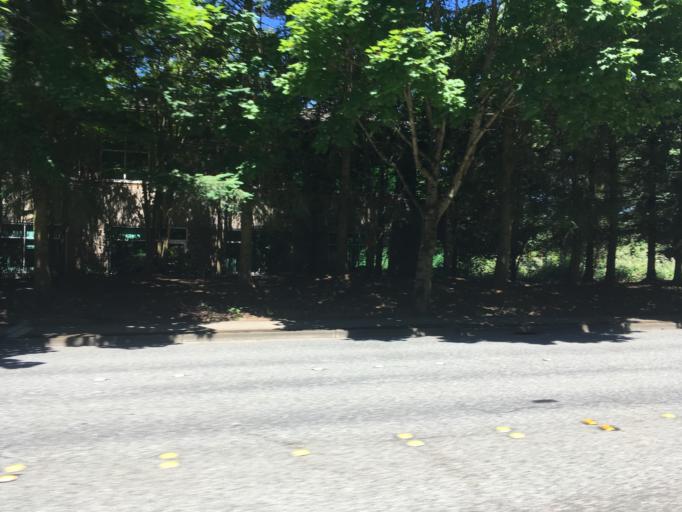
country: US
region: Washington
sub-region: King County
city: Redmond
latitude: 47.6346
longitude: -122.1290
